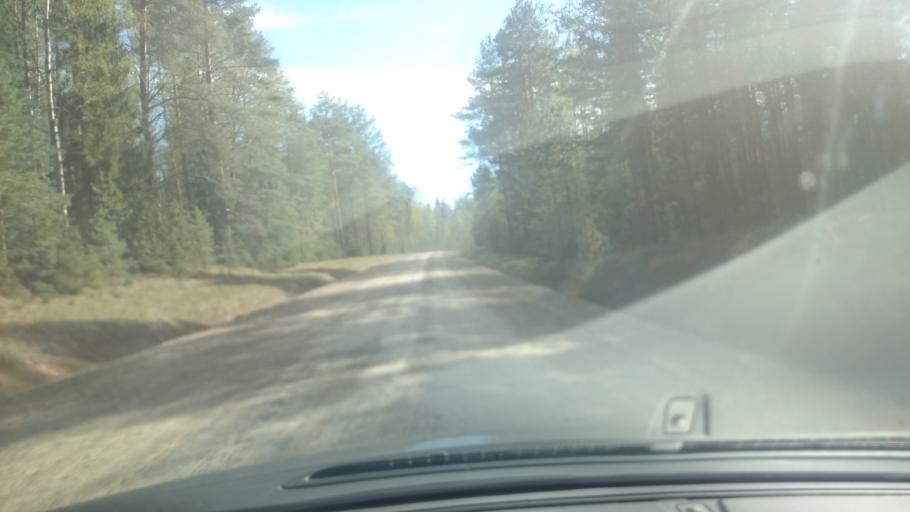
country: EE
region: Ida-Virumaa
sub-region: Sillamaee linn
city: Sillamae
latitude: 59.0794
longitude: 27.7224
